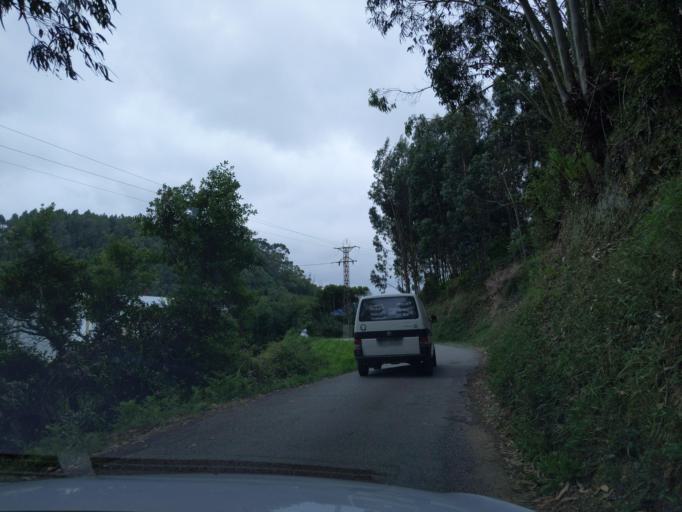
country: ES
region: Asturias
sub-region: Province of Asturias
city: Aviles
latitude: 43.6000
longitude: -5.9114
